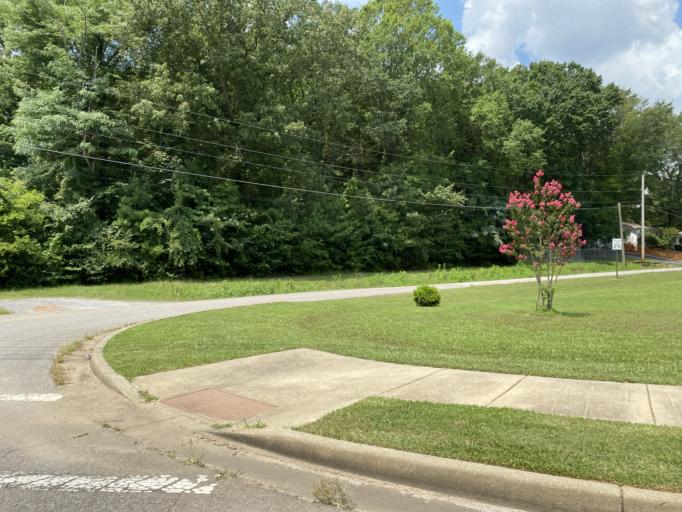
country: US
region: Alabama
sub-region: Madison County
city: Owens Cross Roads
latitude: 34.6531
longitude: -86.4842
